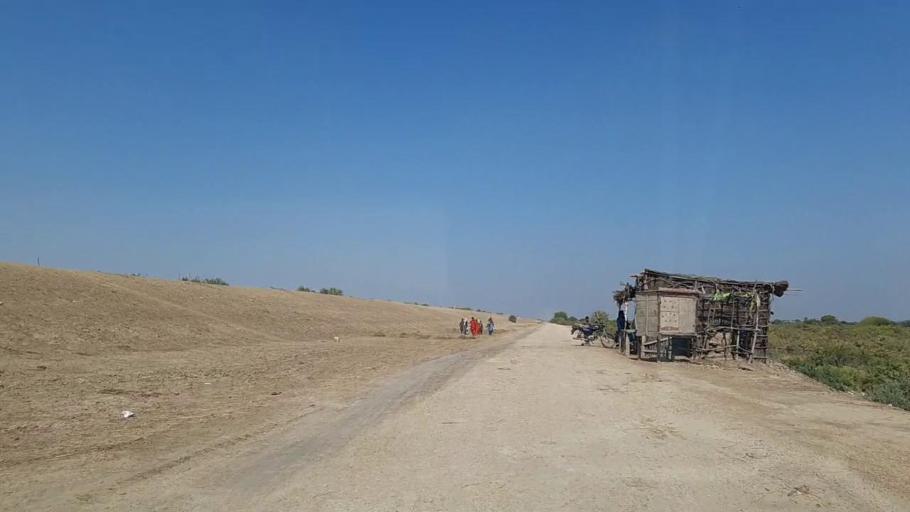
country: PK
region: Sindh
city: Chuhar Jamali
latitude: 24.4593
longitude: 68.0017
